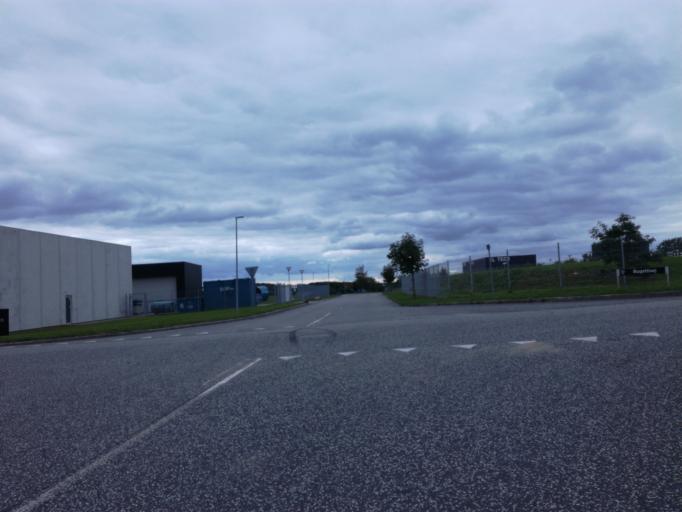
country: DK
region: South Denmark
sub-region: Vejle Kommune
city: Borkop
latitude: 55.6708
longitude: 9.5961
